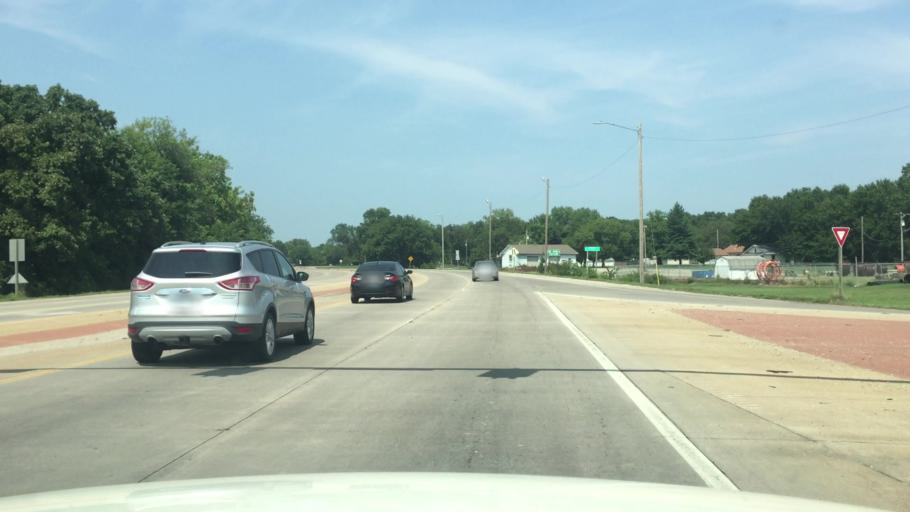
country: US
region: Kansas
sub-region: Crawford County
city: Pittsburg
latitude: 37.4114
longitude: -94.7236
